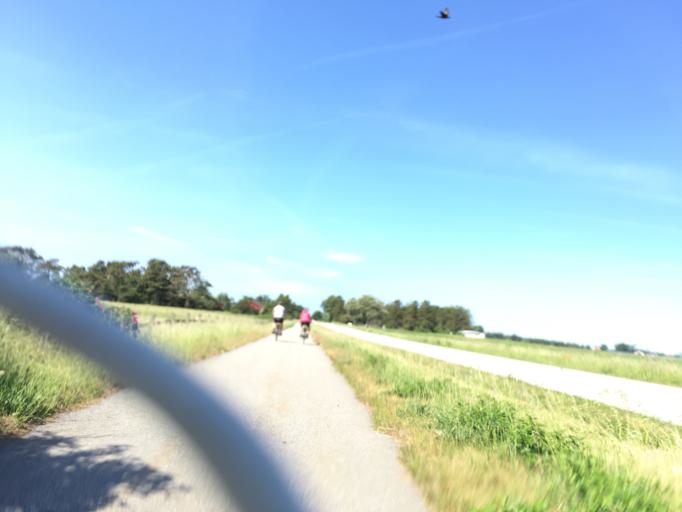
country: SE
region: Skane
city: Smygehamn
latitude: 55.3443
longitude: 13.3000
